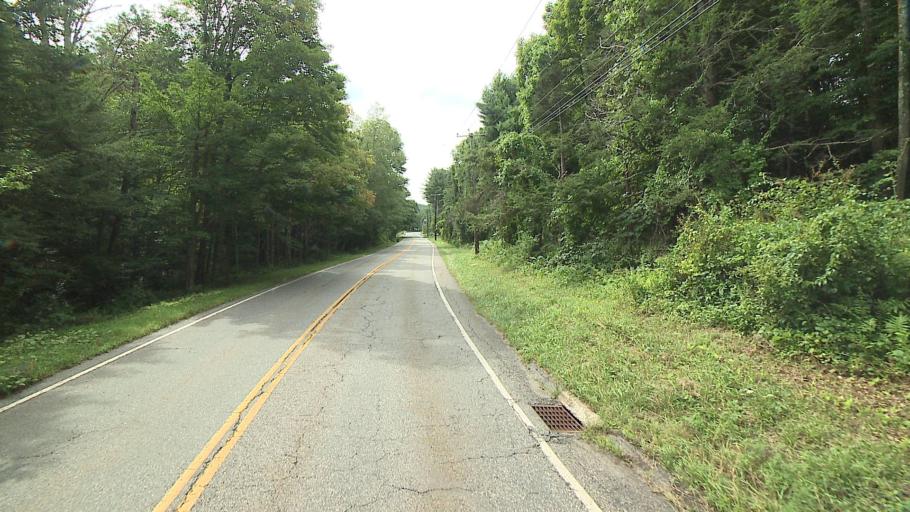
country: US
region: Connecticut
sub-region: Litchfield County
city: New Preston
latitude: 41.6595
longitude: -73.3192
